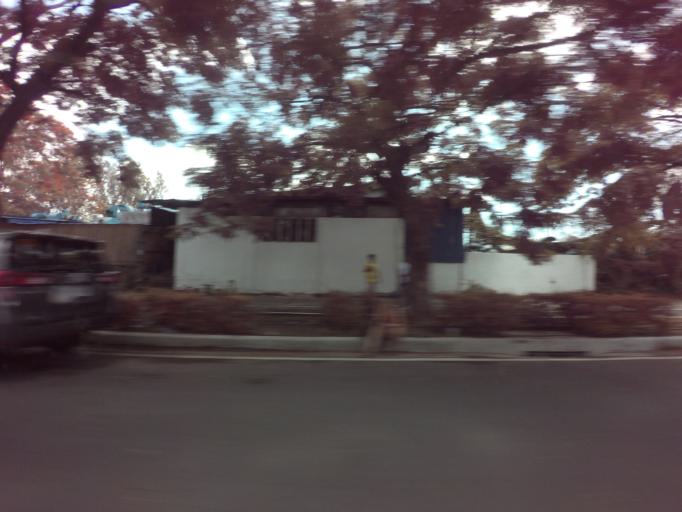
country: PH
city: Sambayanihan People's Village
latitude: 14.4145
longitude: 121.0361
